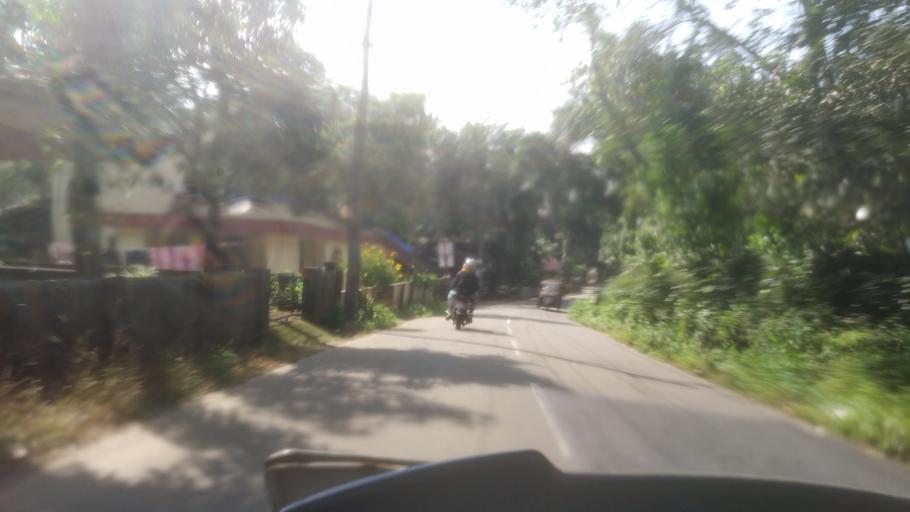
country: IN
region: Kerala
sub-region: Ernakulam
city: Kotamangalam
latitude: 10.0023
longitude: 76.7217
